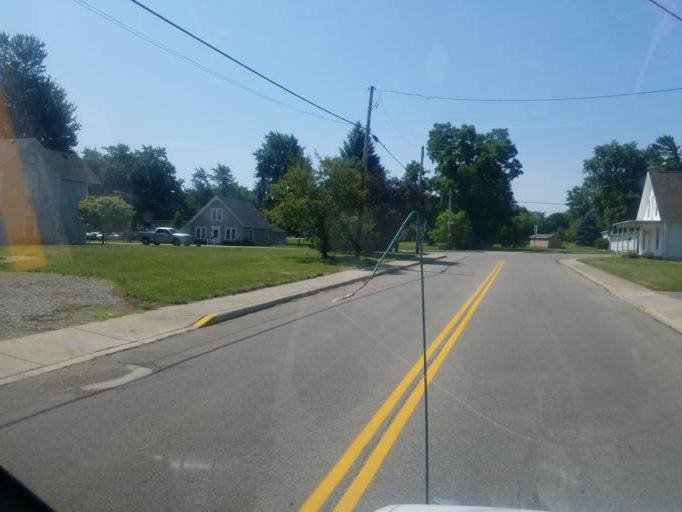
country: US
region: Ohio
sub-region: Champaign County
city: North Lewisburg
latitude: 40.2225
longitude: -83.5586
